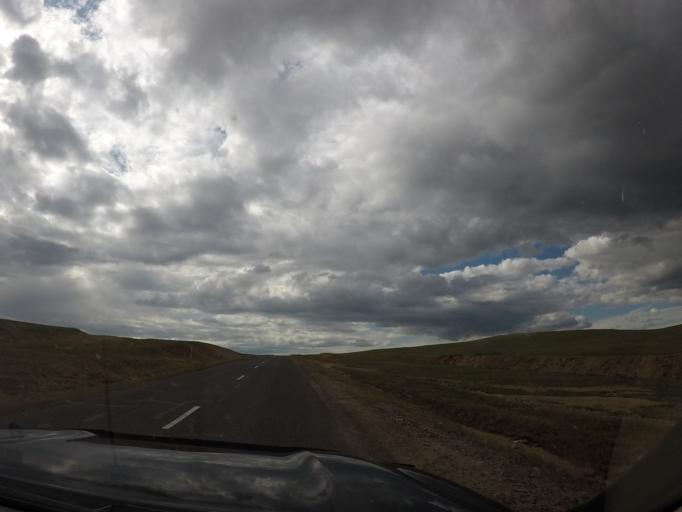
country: MN
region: Hentiy
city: Modot
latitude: 47.5620
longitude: 109.3275
